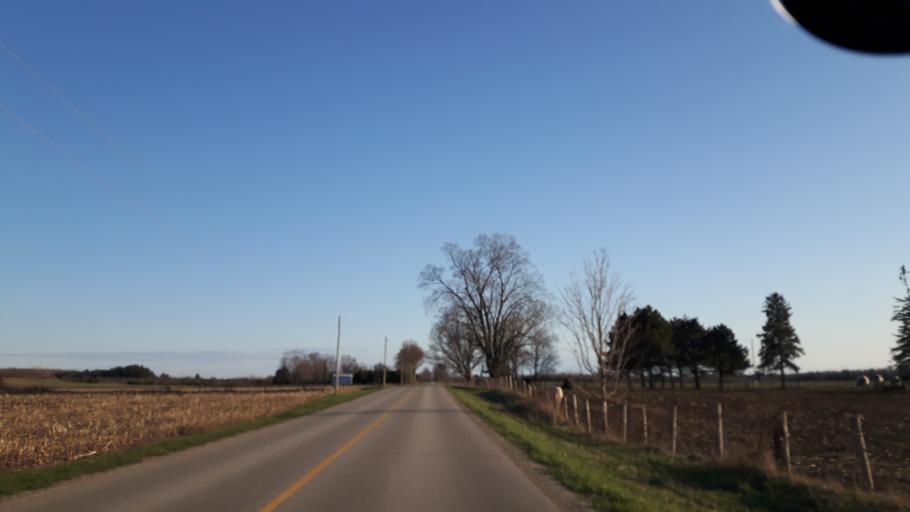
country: CA
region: Ontario
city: Goderich
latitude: 43.6662
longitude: -81.6847
